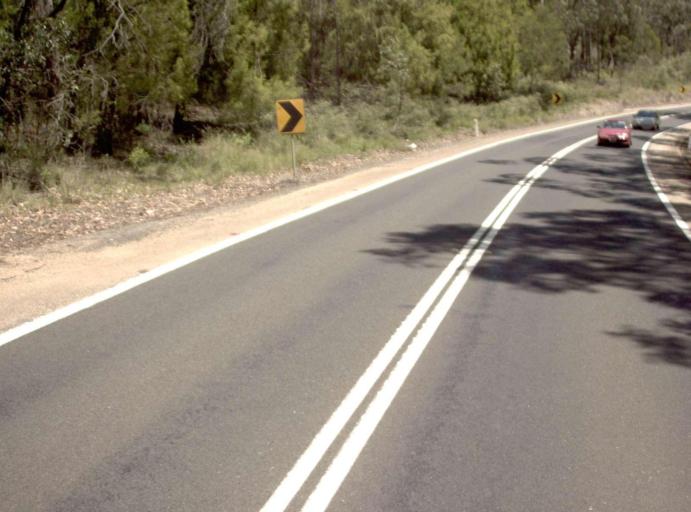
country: AU
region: Victoria
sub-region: East Gippsland
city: Lakes Entrance
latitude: -37.7055
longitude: 148.5764
